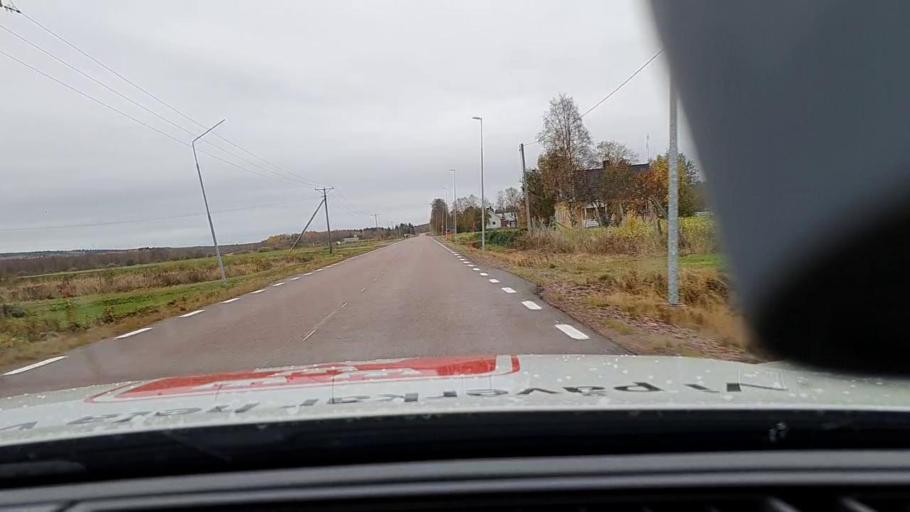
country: FI
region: Lapland
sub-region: Torniolaakso
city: Ylitornio
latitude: 66.1361
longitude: 23.9035
